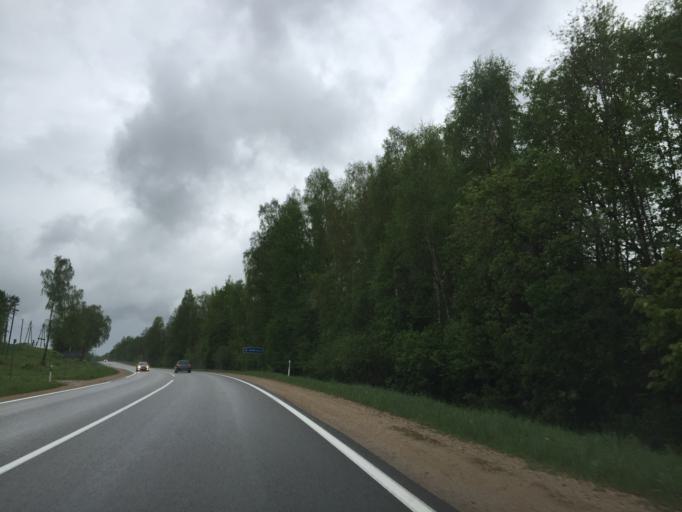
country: LV
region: Kegums
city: Kegums
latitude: 56.7514
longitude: 24.7121
